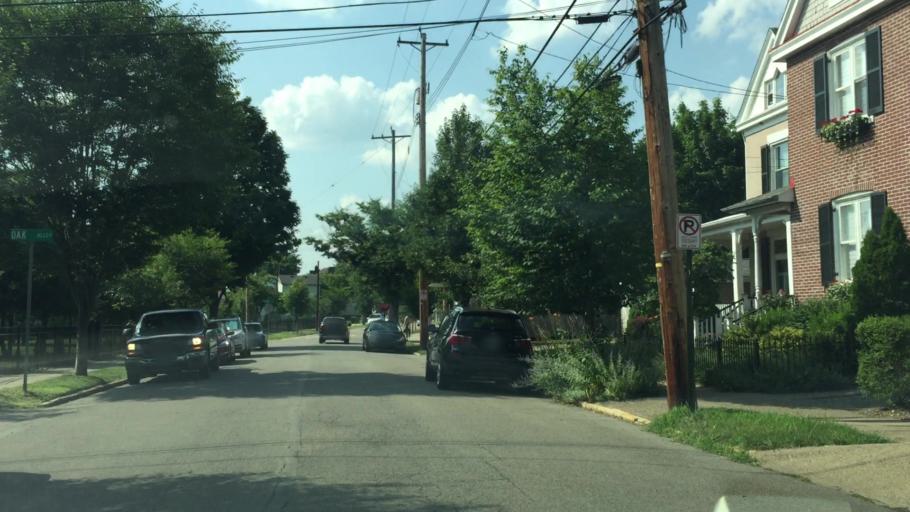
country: US
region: Pennsylvania
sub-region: Allegheny County
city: Sewickley
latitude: 40.5370
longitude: -80.1793
